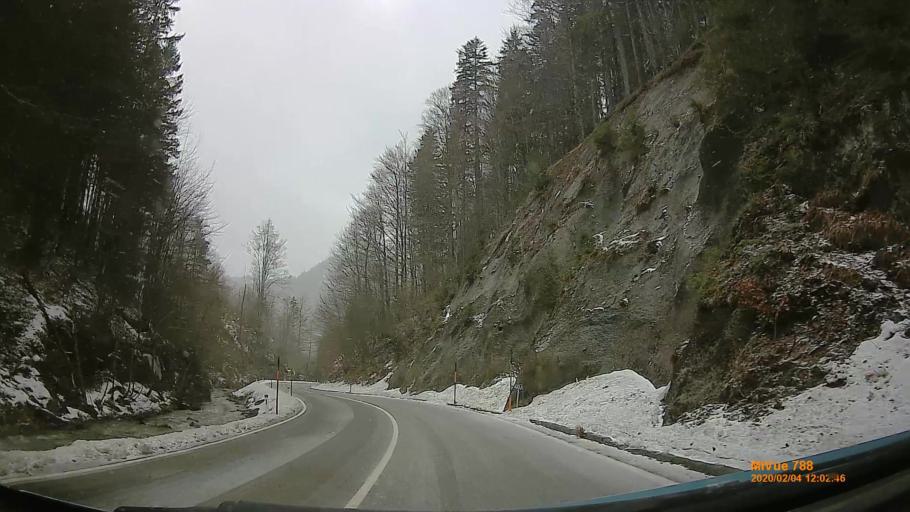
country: AT
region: Styria
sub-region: Politischer Bezirk Bruck-Muerzzuschlag
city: Muerzsteg
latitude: 47.7710
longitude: 15.4587
